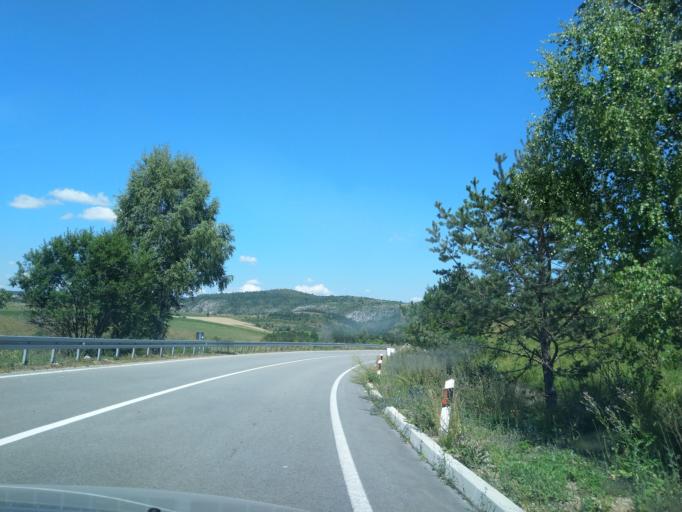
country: RS
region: Central Serbia
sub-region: Zlatiborski Okrug
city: Sjenica
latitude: 43.3218
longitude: 19.8930
